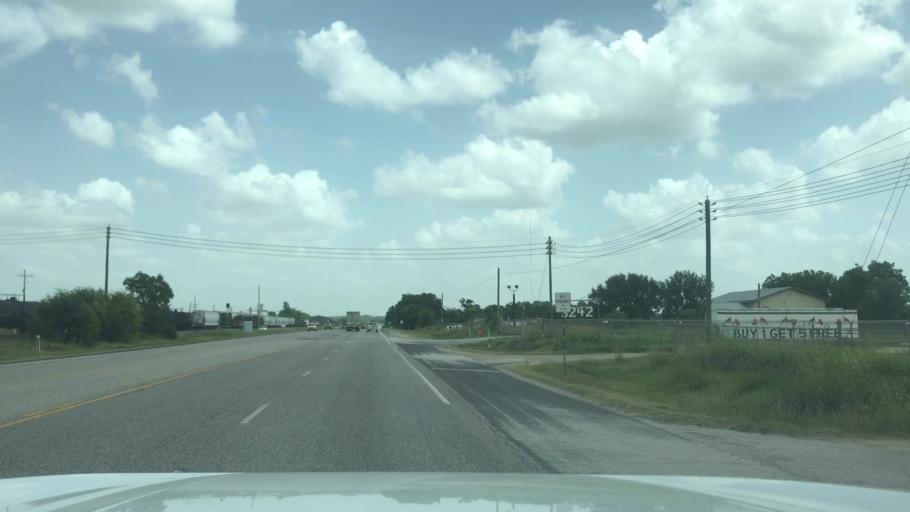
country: US
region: Texas
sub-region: Robertson County
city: Hearne
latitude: 30.8577
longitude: -96.5753
